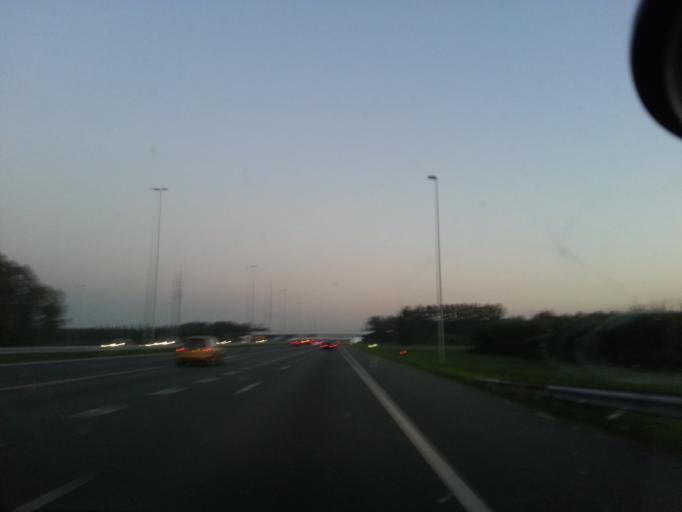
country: NL
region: Utrecht
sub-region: Gemeente Vianen
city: Vianen
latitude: 51.9694
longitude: 5.1094
